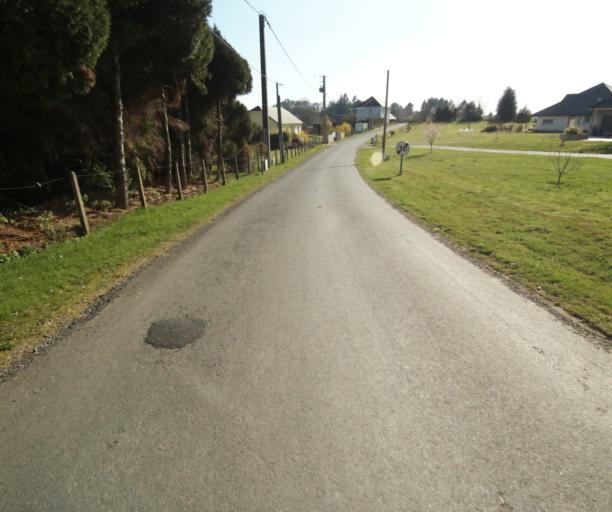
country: FR
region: Limousin
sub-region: Departement de la Correze
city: Saint-Clement
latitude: 45.3000
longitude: 1.6923
